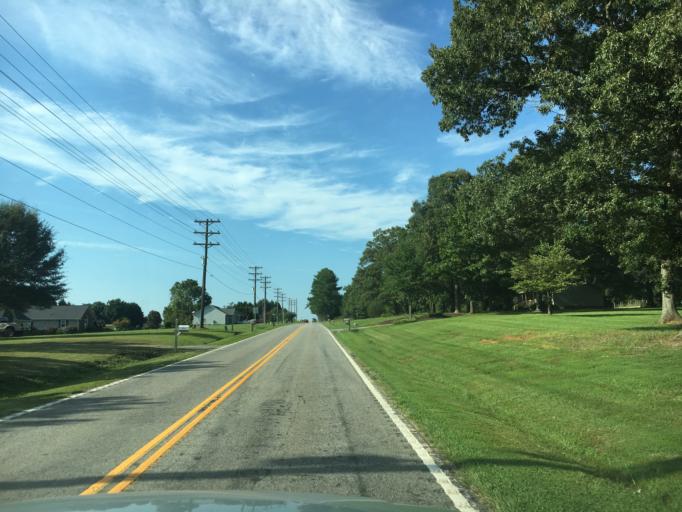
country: US
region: South Carolina
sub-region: Spartanburg County
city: Boiling Springs
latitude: 35.0756
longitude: -81.9289
